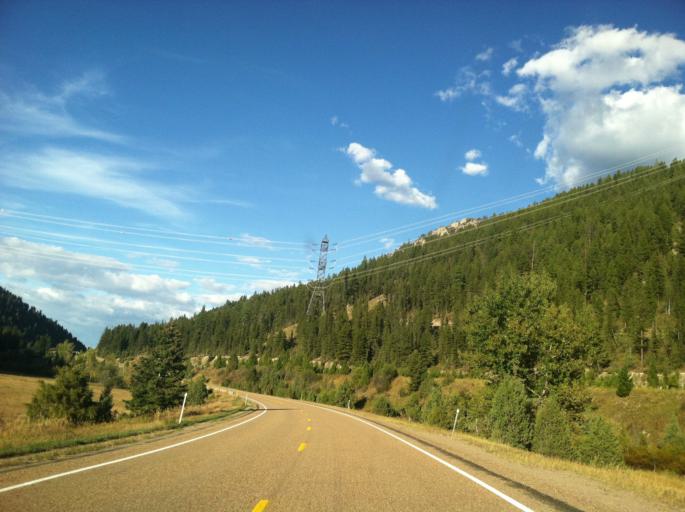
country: US
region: Montana
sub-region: Granite County
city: Philipsburg
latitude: 46.4418
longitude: -113.2551
